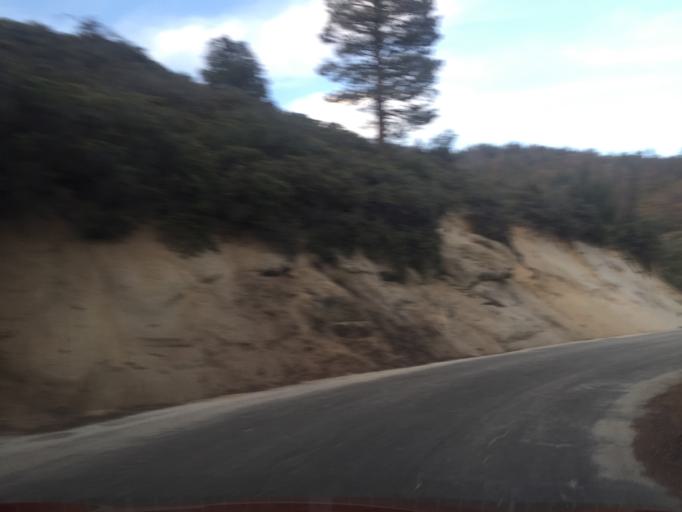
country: US
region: California
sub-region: Tulare County
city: Three Rivers
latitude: 36.4493
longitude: -118.7040
